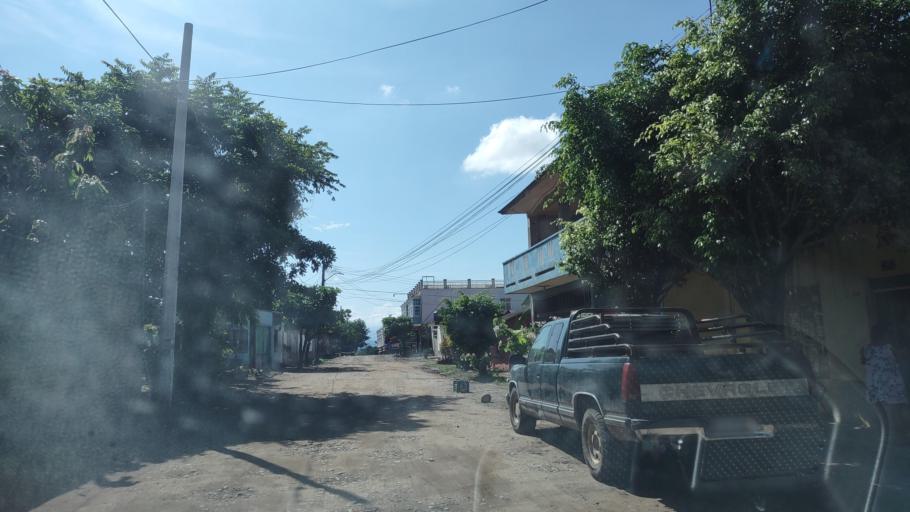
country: MX
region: Veracruz
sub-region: Martinez de la Torre
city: La Union Paso Largo
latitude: 20.1290
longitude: -96.9941
